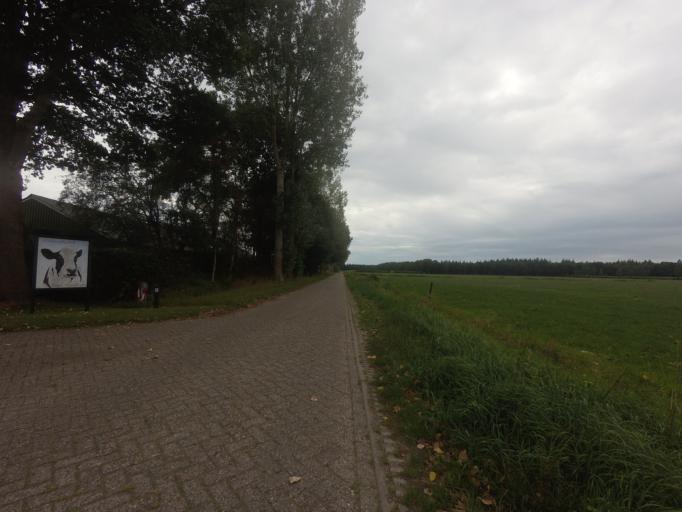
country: NL
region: Overijssel
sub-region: Gemeente Raalte
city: Raalte
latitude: 52.3576
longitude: 6.3194
